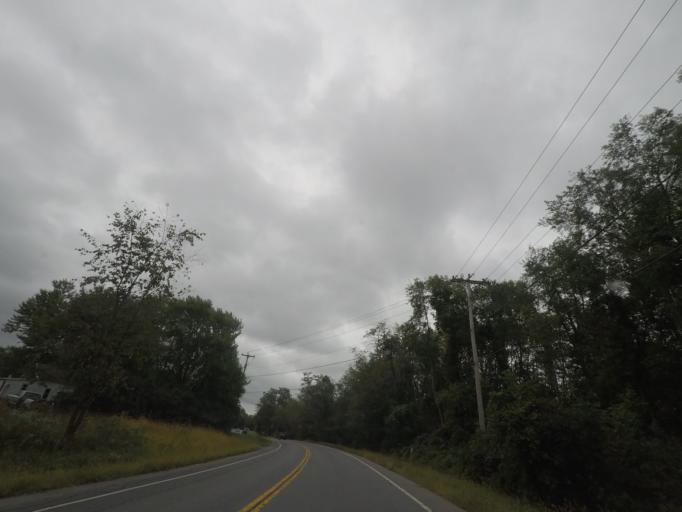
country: US
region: New York
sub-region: Saratoga County
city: Country Knolls
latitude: 42.9317
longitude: -73.7673
